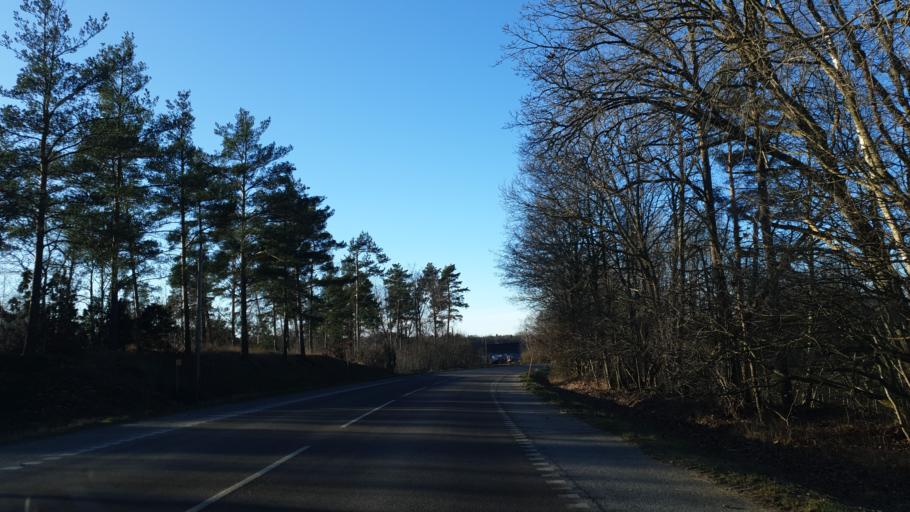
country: SE
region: Blekinge
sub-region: Ronneby Kommun
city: Ronneby
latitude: 56.1920
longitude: 15.3584
